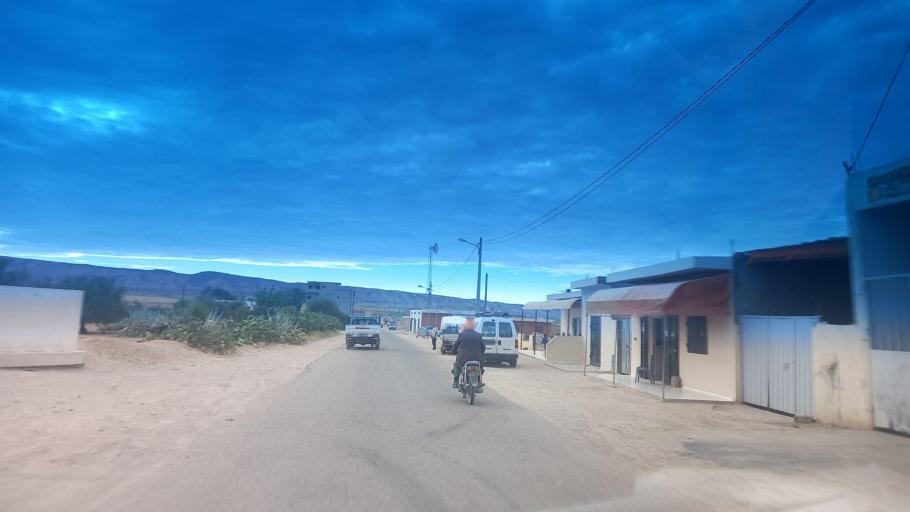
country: TN
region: Al Qasrayn
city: Sbiba
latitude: 35.3634
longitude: 9.0888
